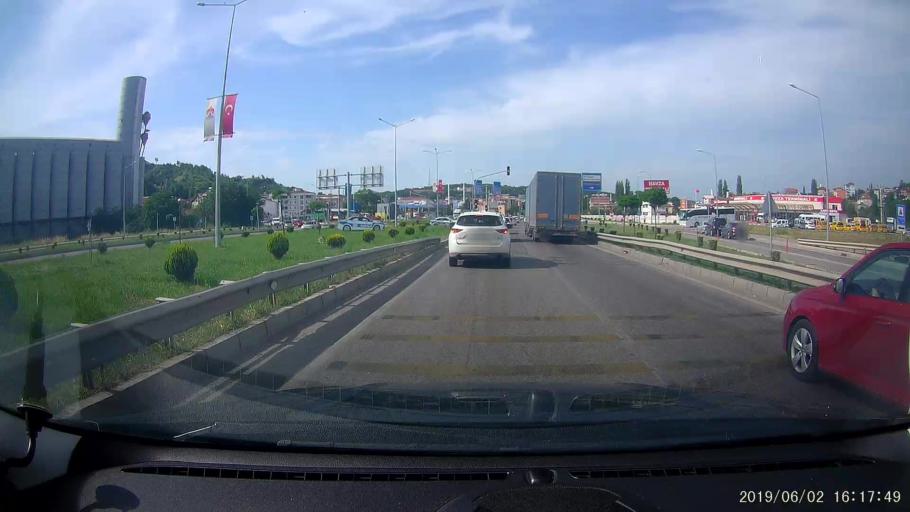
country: TR
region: Samsun
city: Havza
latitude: 40.9607
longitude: 35.6662
